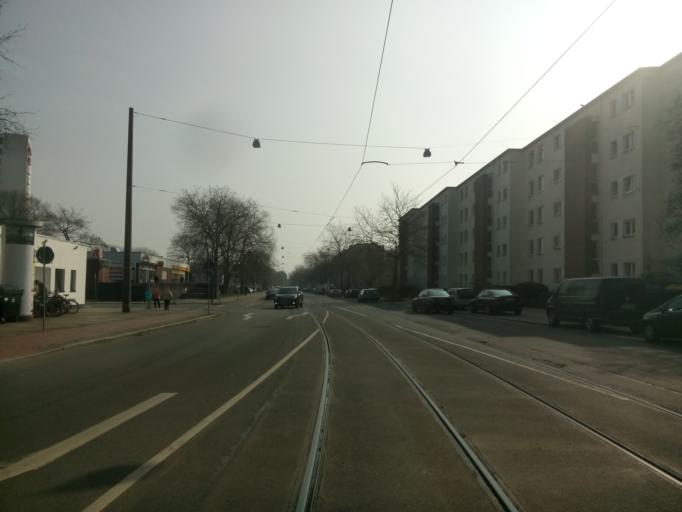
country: DE
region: Lower Saxony
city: Lilienthal
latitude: 53.0784
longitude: 8.9040
